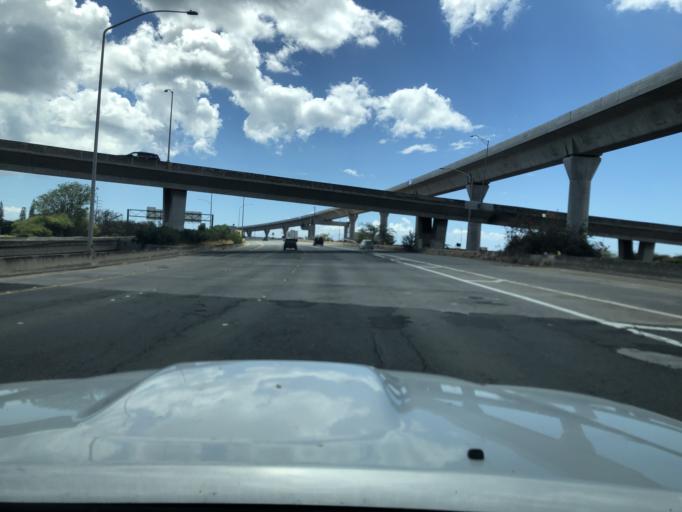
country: US
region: Hawaii
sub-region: Honolulu County
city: Hickam Field
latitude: 21.3433
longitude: -157.9327
